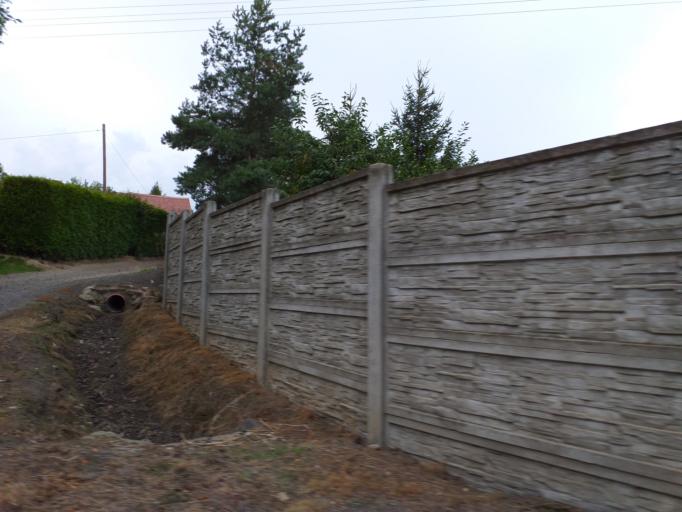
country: PL
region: Lower Silesian Voivodeship
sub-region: Powiat lubanski
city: Lesna
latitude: 51.0184
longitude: 15.3139
